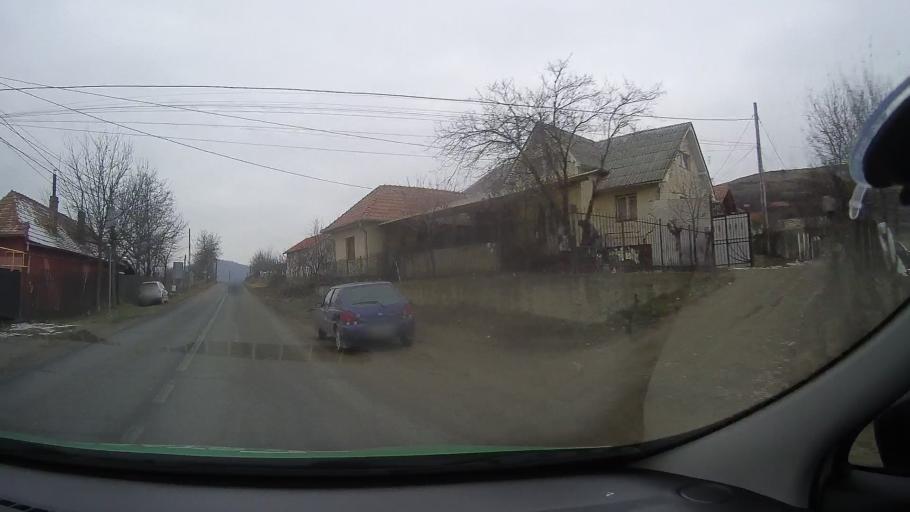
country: RO
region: Alba
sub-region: Comuna Ighiu
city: Sard
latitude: 46.1213
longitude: 23.5138
